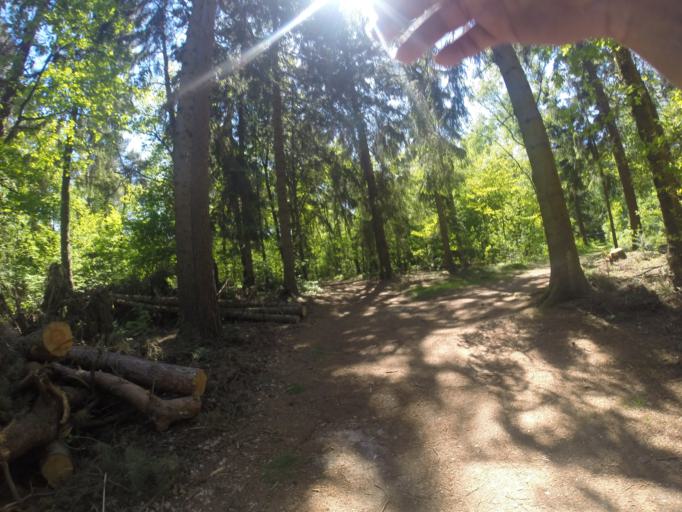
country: NL
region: Gelderland
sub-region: Gemeente Montferland
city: s-Heerenberg
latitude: 51.9024
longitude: 6.2088
